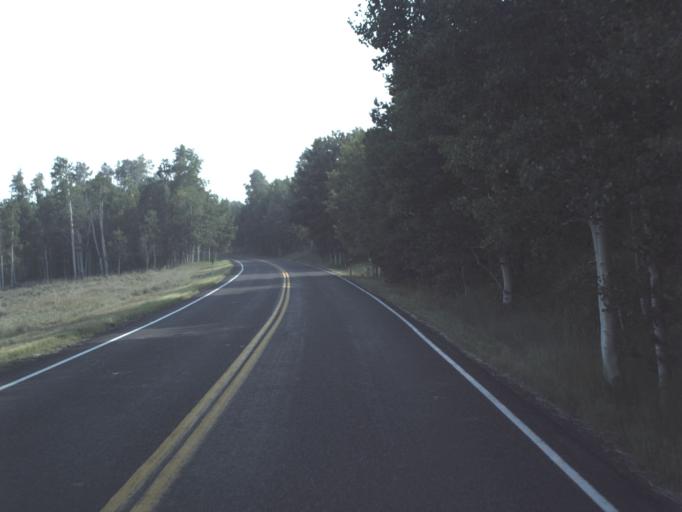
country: US
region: Wyoming
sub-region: Uinta County
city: Evanston
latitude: 40.8581
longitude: -110.8433
